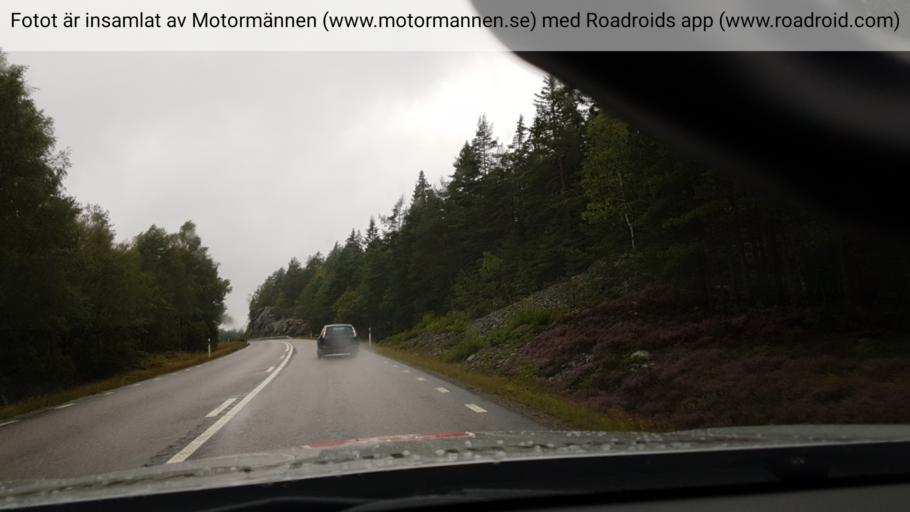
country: SE
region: Vaestra Goetaland
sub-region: Dals-Ed Kommun
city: Ed
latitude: 58.8751
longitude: 11.8547
